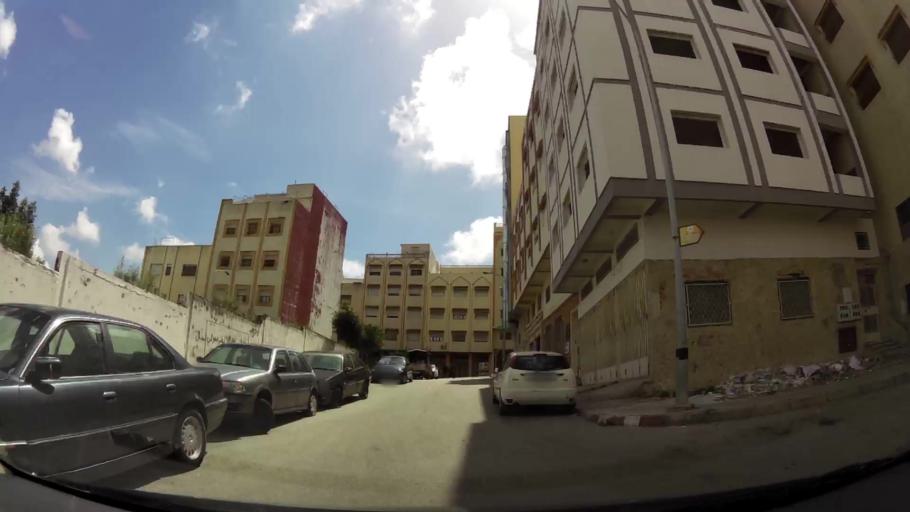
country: MA
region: Tanger-Tetouan
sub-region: Tanger-Assilah
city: Tangier
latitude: 35.7563
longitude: -5.8267
